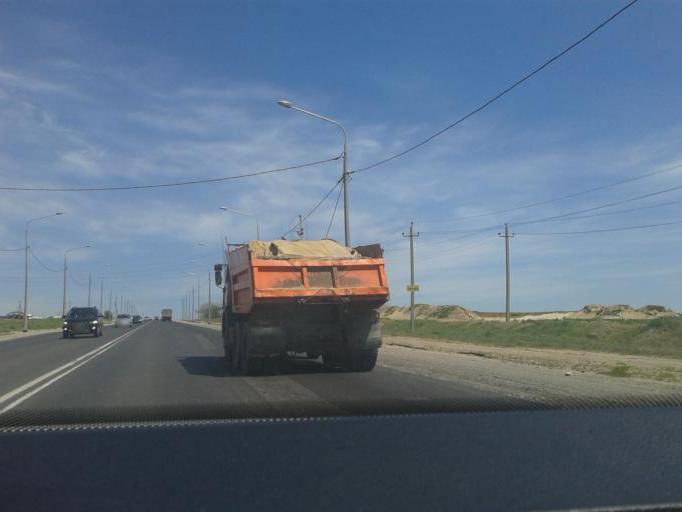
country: RU
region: Volgograd
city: Vodstroy
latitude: 48.8105
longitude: 44.5238
